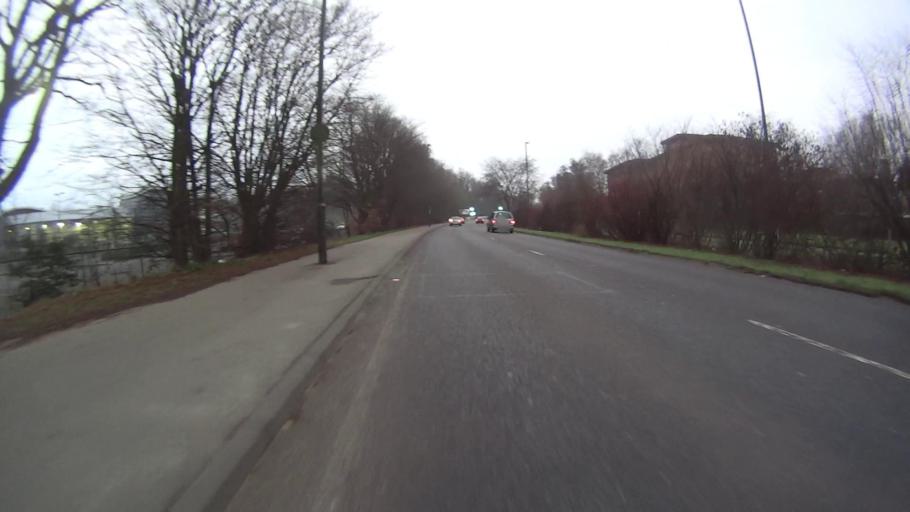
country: GB
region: England
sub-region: West Sussex
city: Broadfield
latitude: 51.0983
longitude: -0.1930
